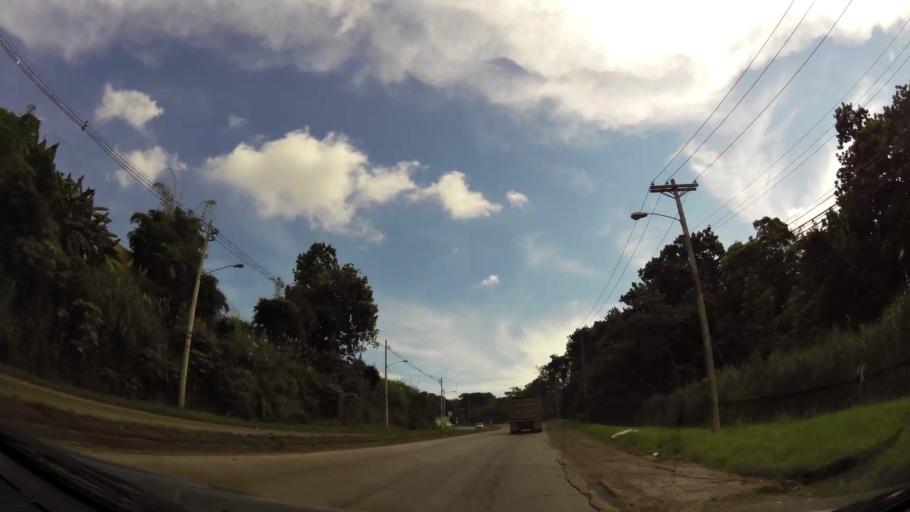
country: PA
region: Panama
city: Panama
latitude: 9.0369
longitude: -79.5426
